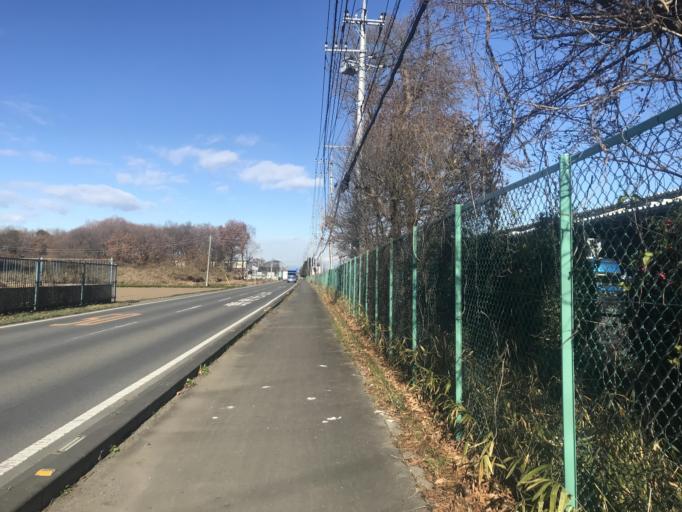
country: JP
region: Ibaraki
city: Yuki
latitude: 36.3464
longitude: 139.8785
